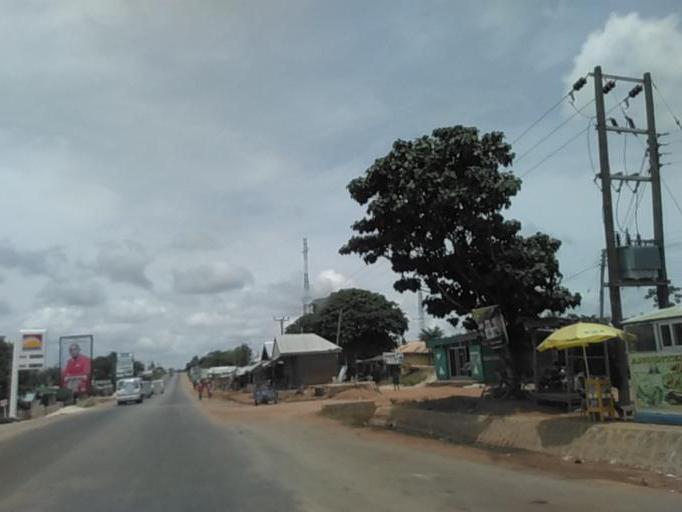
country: GH
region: Ashanti
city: Mamponteng
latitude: 6.8356
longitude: -1.5162
